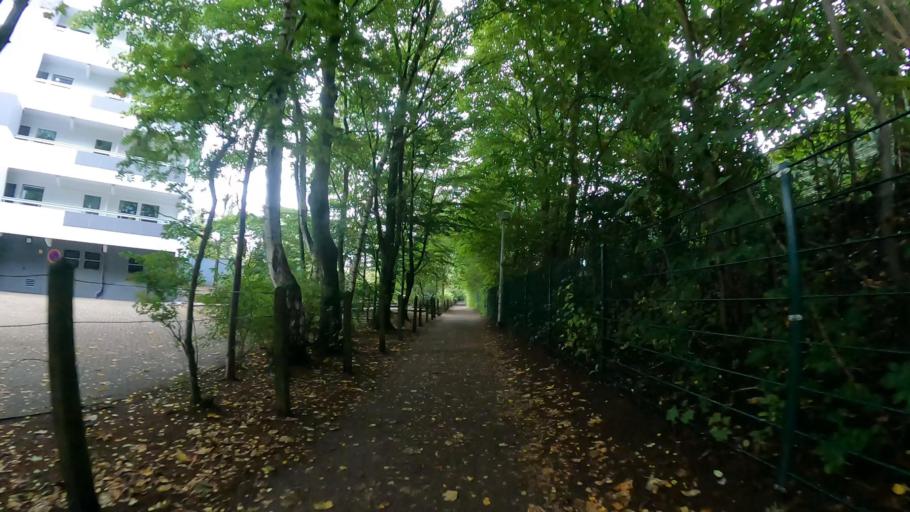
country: DE
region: Schleswig-Holstein
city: Rellingen
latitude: 53.6513
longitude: 9.8030
